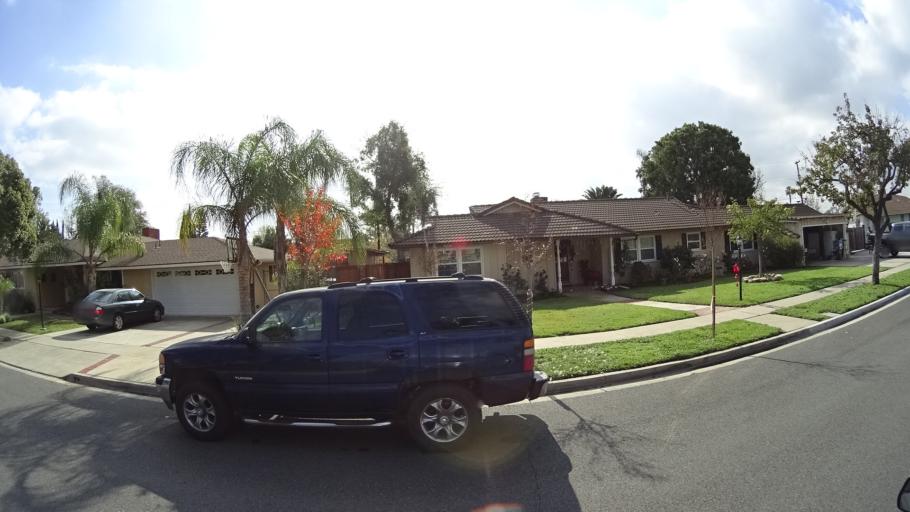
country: US
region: California
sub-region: Orange County
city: Tustin
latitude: 33.7557
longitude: -117.8206
